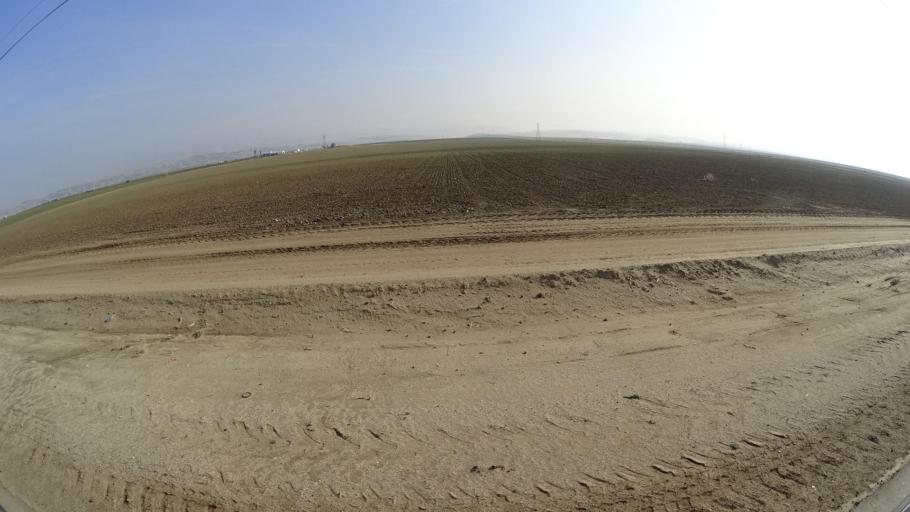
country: US
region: California
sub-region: Kern County
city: Arvin
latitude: 35.0832
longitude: -118.8465
